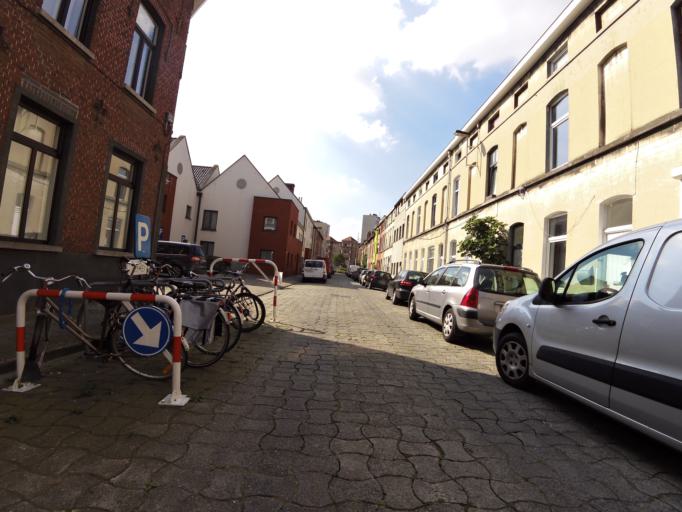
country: BE
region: Flanders
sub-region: Provincie Oost-Vlaanderen
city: Gent
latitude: 51.0609
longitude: 3.7173
